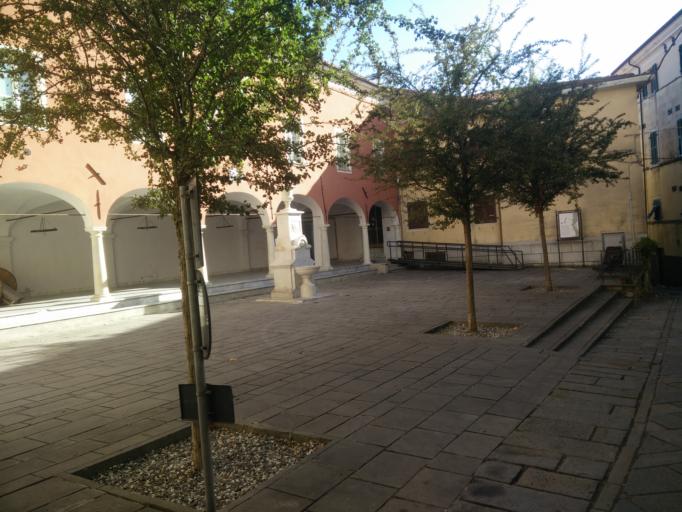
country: IT
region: Tuscany
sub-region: Provincia di Massa-Carrara
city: Fosdinovo
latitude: 44.1347
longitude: 10.0194
